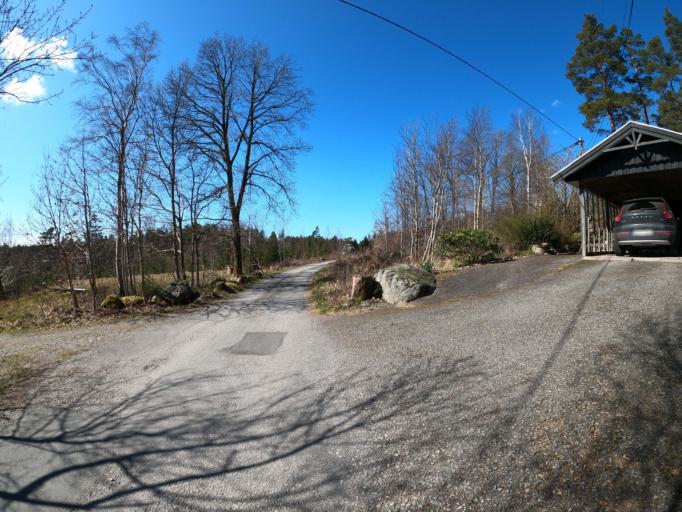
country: SE
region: Vaestra Goetaland
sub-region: Harryda Kommun
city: Molnlycke
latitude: 57.6337
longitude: 12.1231
